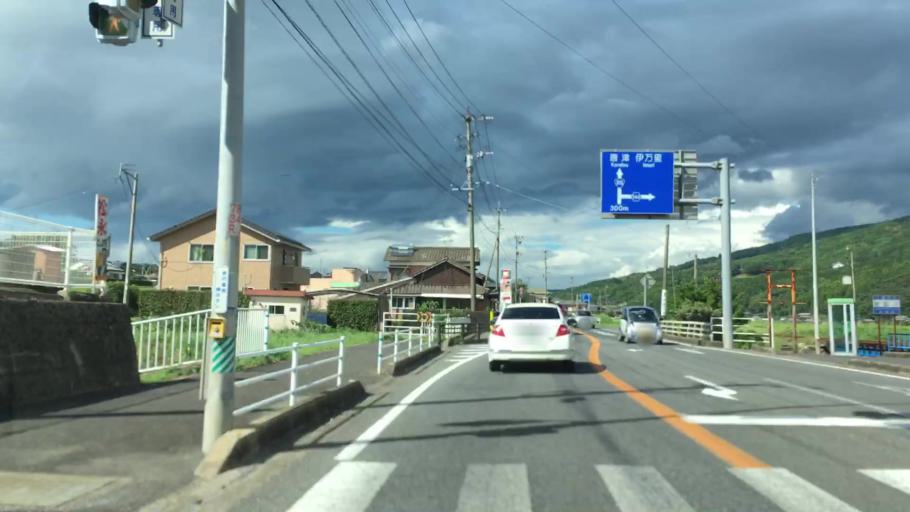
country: JP
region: Saga Prefecture
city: Imaricho-ko
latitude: 33.2258
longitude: 129.8472
